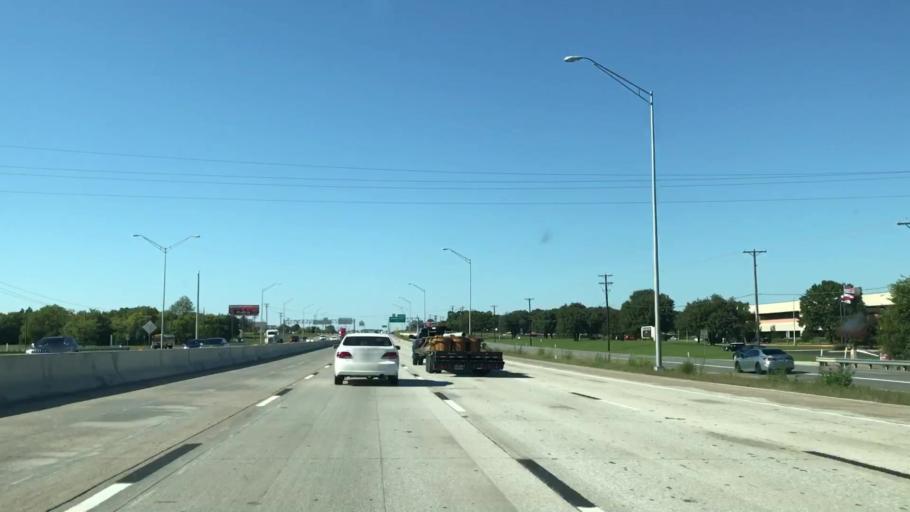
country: US
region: Texas
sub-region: Denton County
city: Hickory Creek
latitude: 33.1344
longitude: -97.0440
